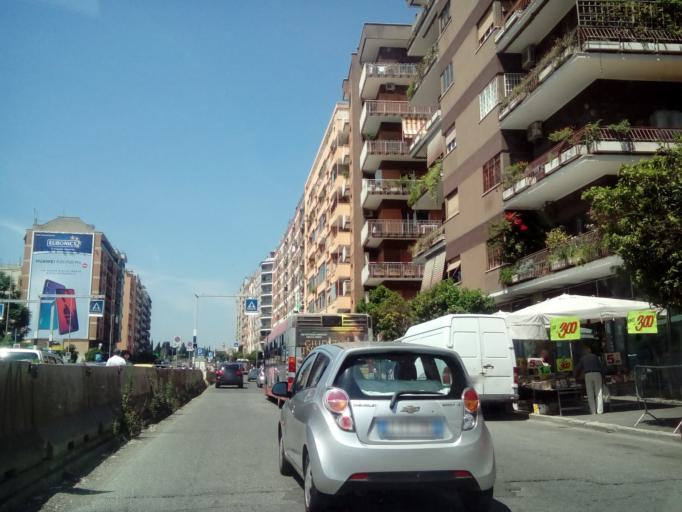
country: IT
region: Latium
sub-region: Citta metropolitana di Roma Capitale
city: Rome
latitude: 41.9086
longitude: 12.5387
